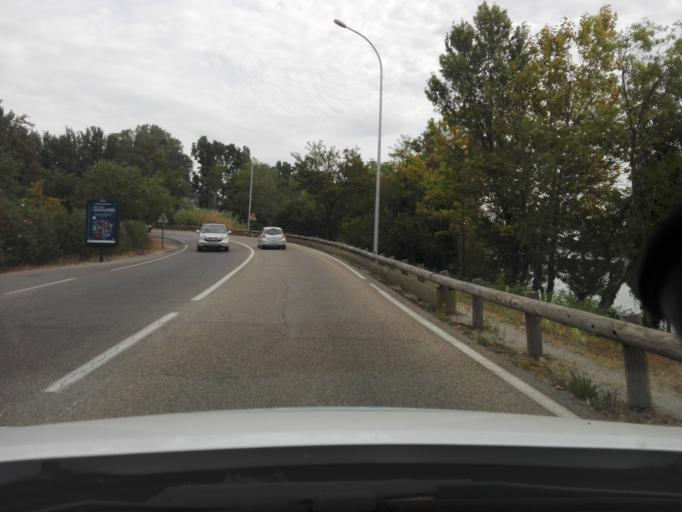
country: FR
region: Languedoc-Roussillon
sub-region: Departement du Gard
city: Villeneuve-les-Avignon
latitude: 43.9543
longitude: 4.7926
